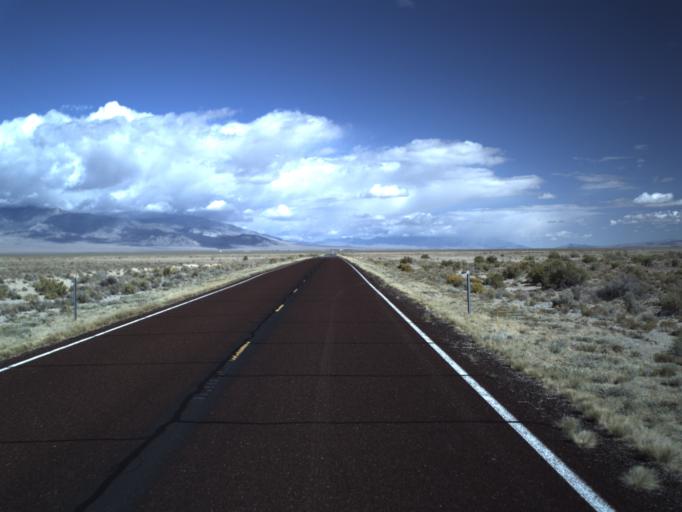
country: US
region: Nevada
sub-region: White Pine County
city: McGill
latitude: 38.9581
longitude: -114.0334
